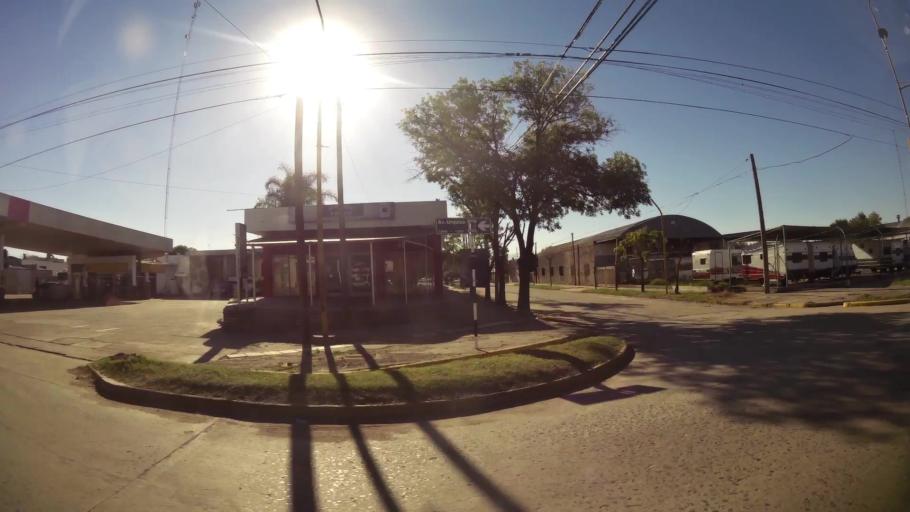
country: AR
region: Cordoba
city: San Francisco
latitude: -31.4159
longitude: -62.0944
